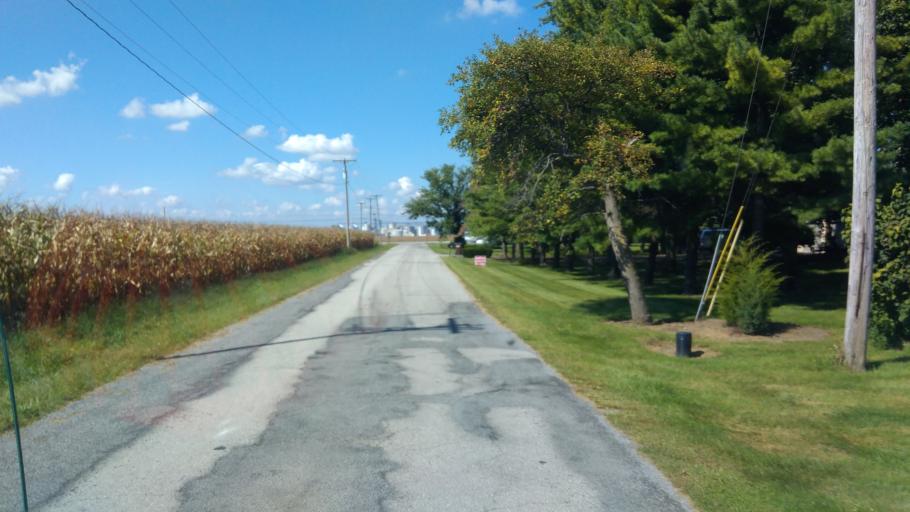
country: US
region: Ohio
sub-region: Marion County
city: Marion
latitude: 40.6271
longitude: -83.1350
